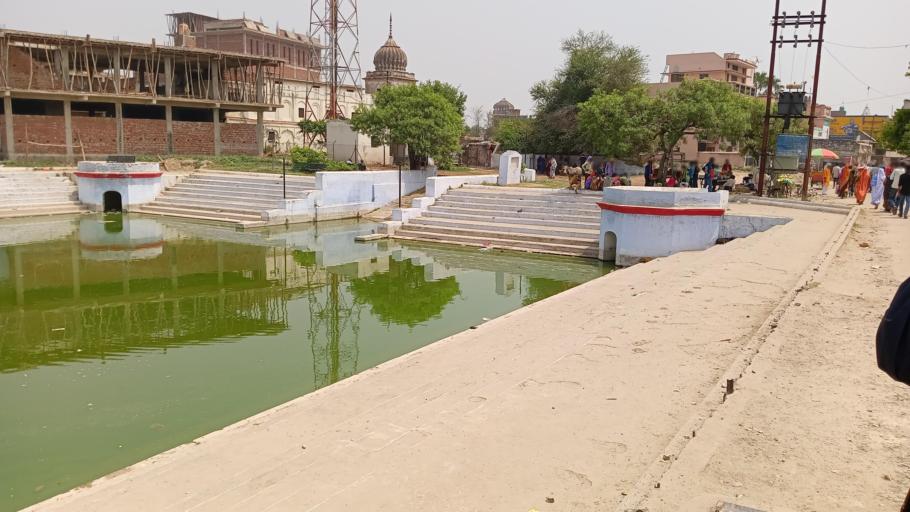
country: IN
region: Uttar Pradesh
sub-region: Faizabad
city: Ayodhya
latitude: 26.7942
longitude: 82.2036
